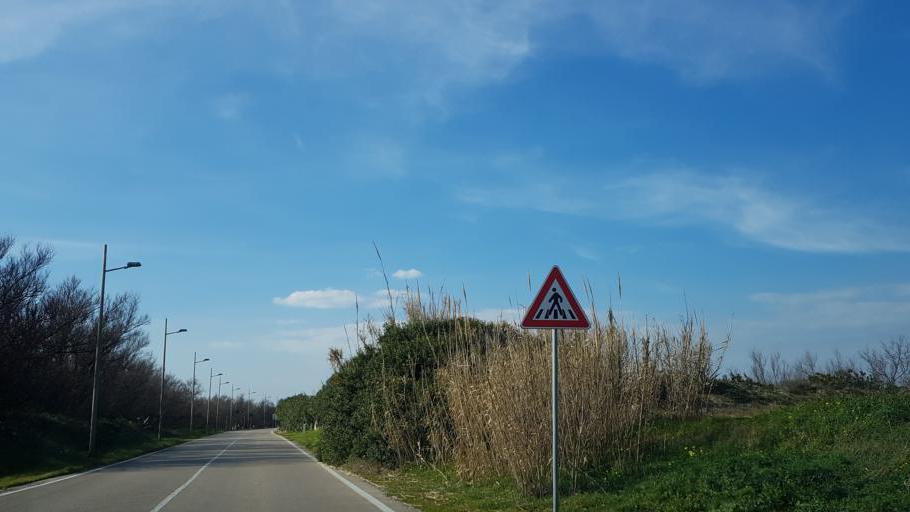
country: IT
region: Apulia
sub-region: Provincia di Brindisi
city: Brindisi
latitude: 40.6888
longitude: 17.8477
